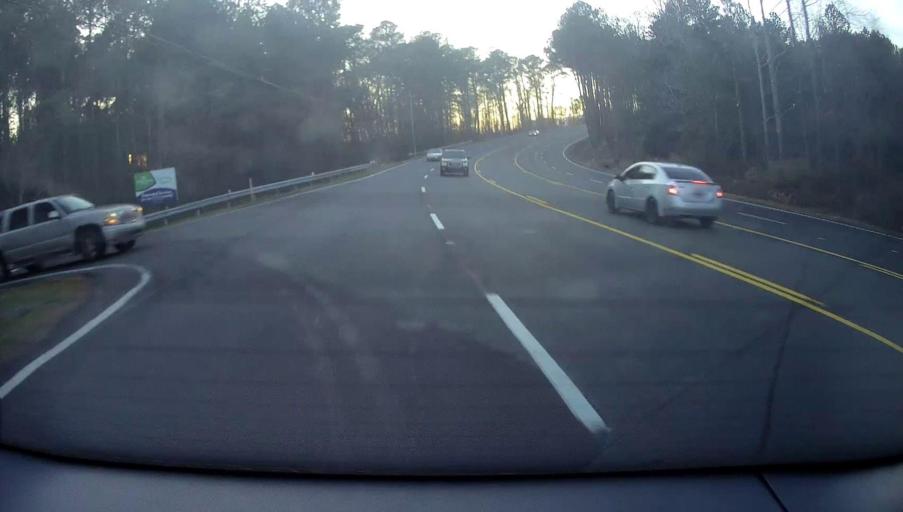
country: US
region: Georgia
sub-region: Fulton County
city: Union City
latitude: 33.5592
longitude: -84.5139
